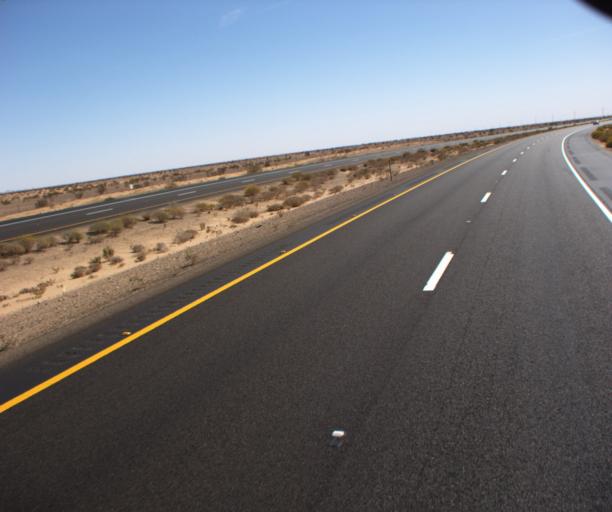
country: US
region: Arizona
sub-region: Yuma County
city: Somerton
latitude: 32.5034
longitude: -114.5587
